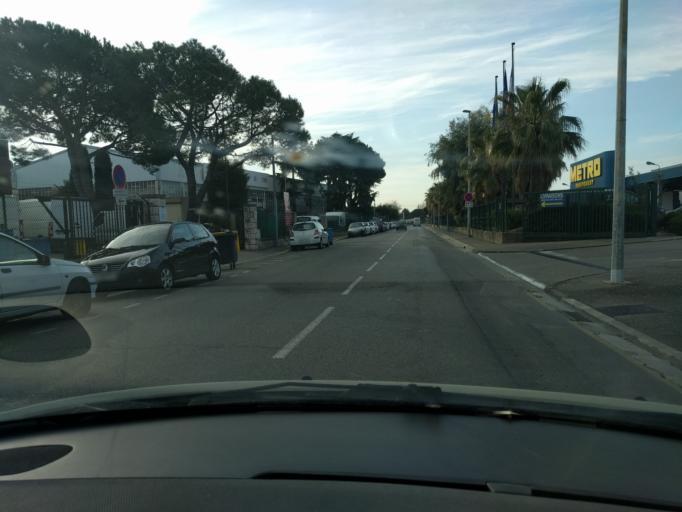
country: FR
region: Provence-Alpes-Cote d'Azur
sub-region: Departement des Alpes-Maritimes
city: Mandelieu-la-Napoule
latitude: 43.5481
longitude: 6.9656
